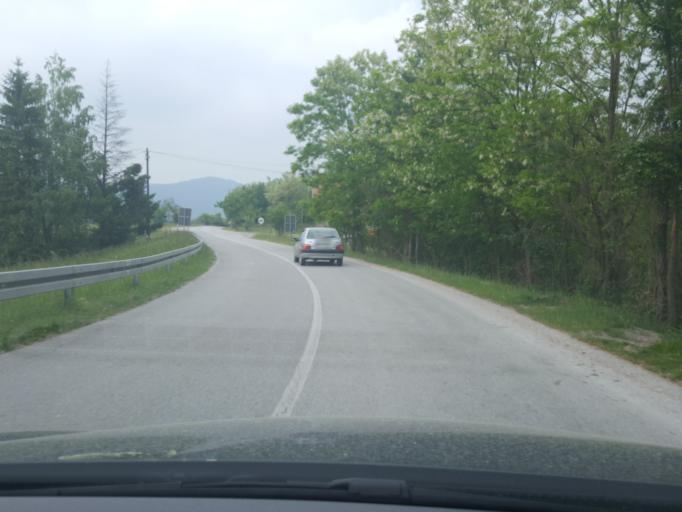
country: RS
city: Kamenica
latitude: 44.2065
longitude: 19.7181
